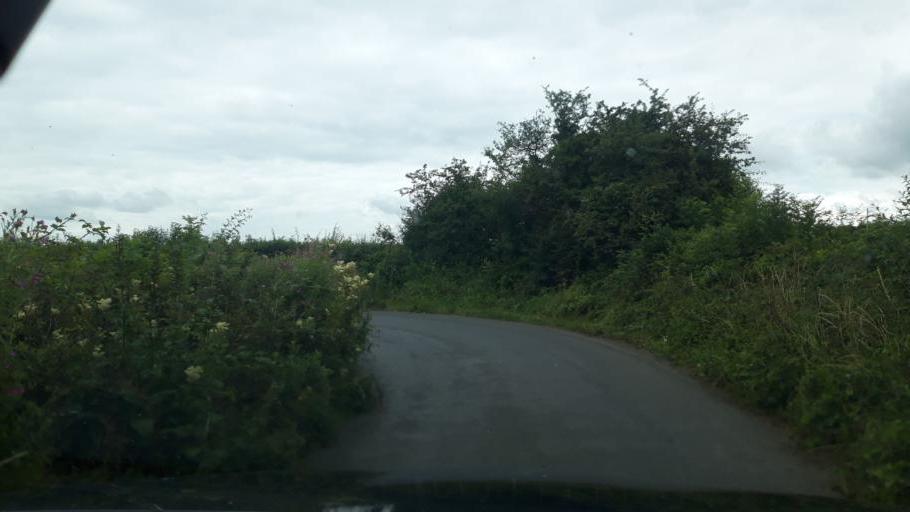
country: IE
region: Leinster
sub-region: Kilkenny
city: Graiguenamanagh
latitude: 52.5953
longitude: -7.0296
